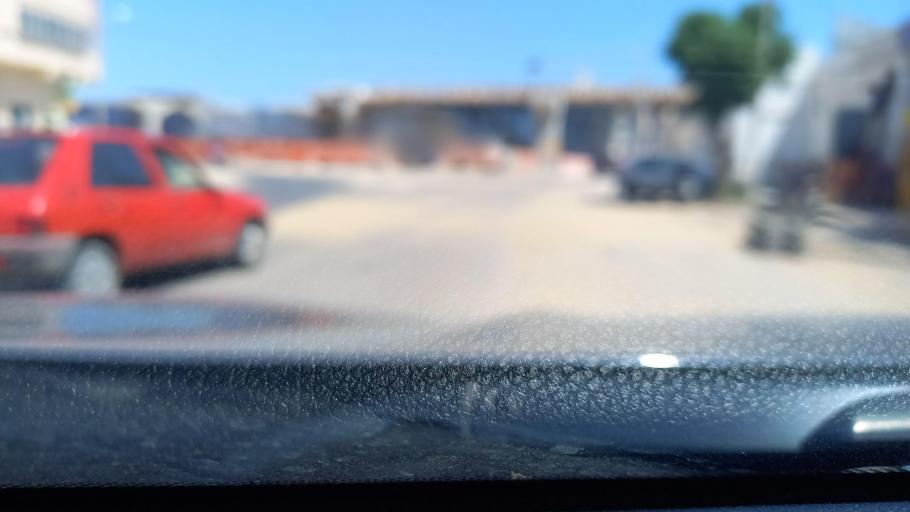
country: TN
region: Safaqis
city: Sfax
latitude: 34.7463
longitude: 10.7255
